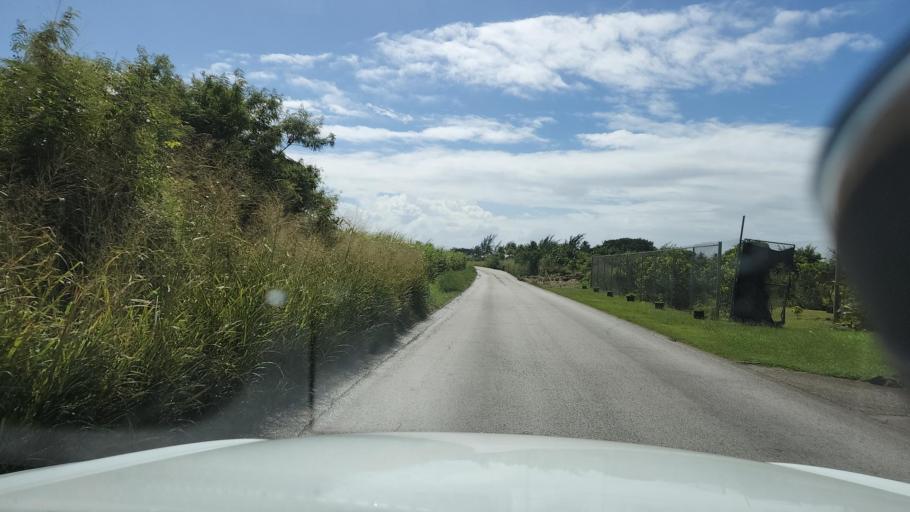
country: BB
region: Christ Church
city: Oistins
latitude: 13.0909
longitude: -59.5293
